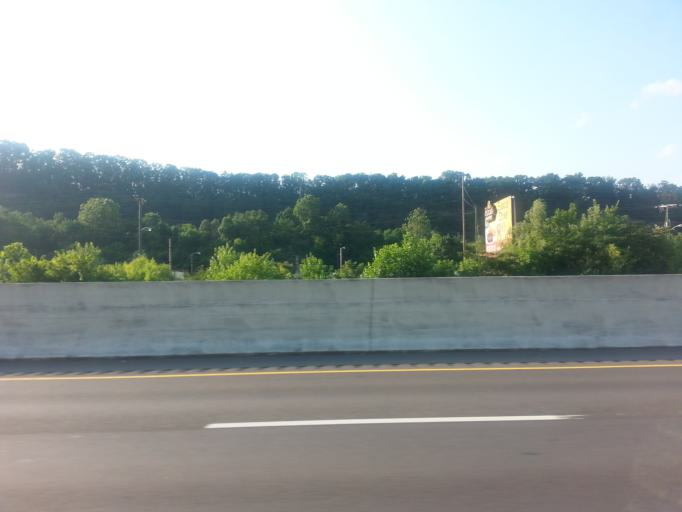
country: US
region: Tennessee
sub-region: Knox County
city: Knoxville
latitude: 36.0158
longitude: -83.9278
